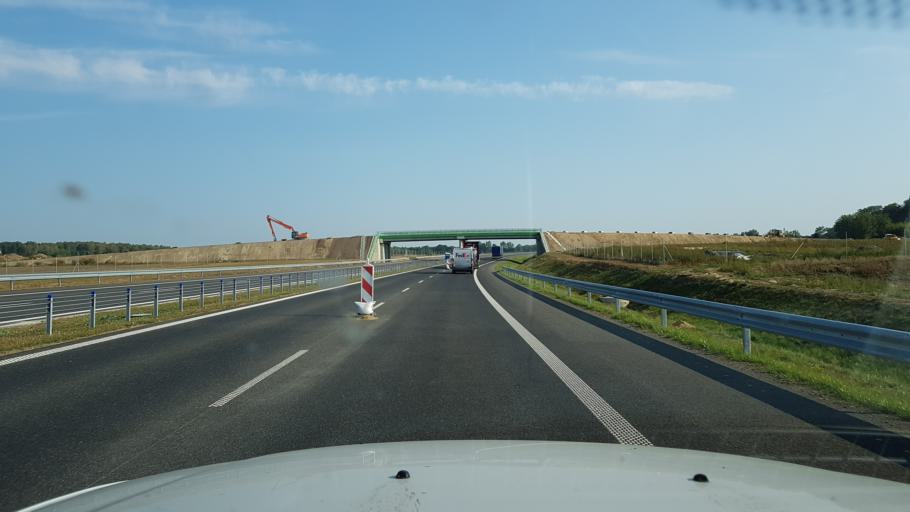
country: PL
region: West Pomeranian Voivodeship
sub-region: Powiat gryficki
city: Ploty
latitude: 53.7728
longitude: 15.2374
